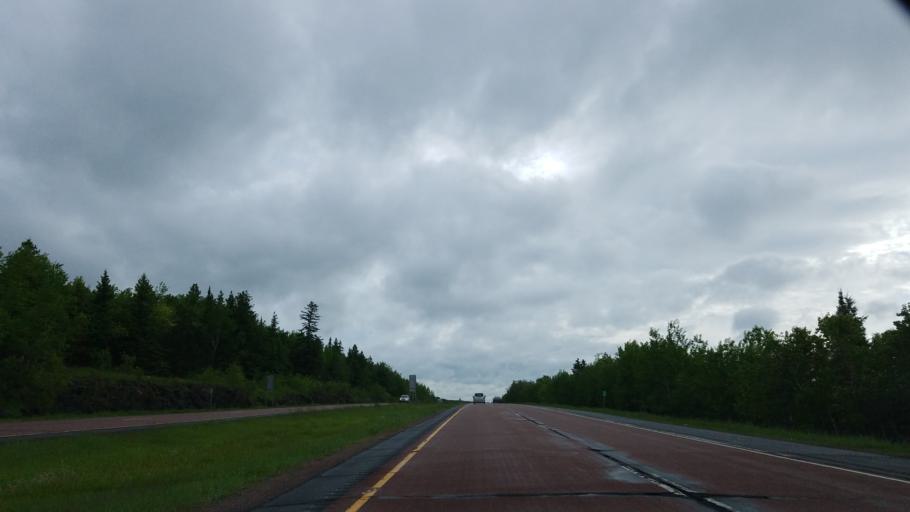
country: US
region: Minnesota
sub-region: Saint Louis County
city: Arnold
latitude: 46.8486
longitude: -91.9933
